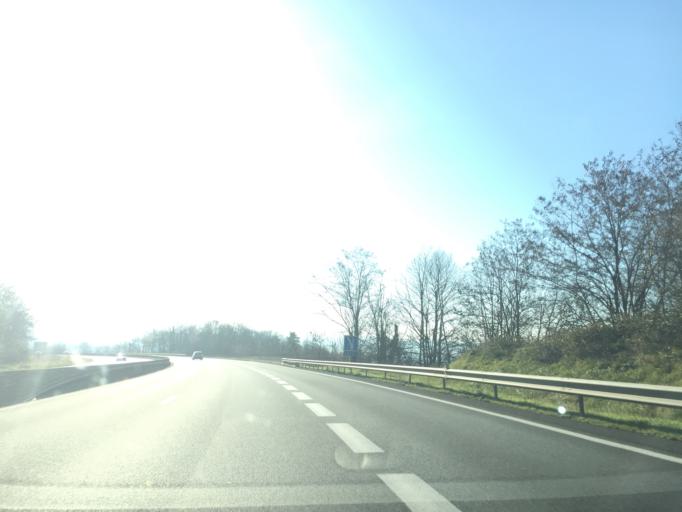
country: FR
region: Limousin
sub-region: Departement de la Correze
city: Donzenac
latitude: 45.2447
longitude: 1.5140
